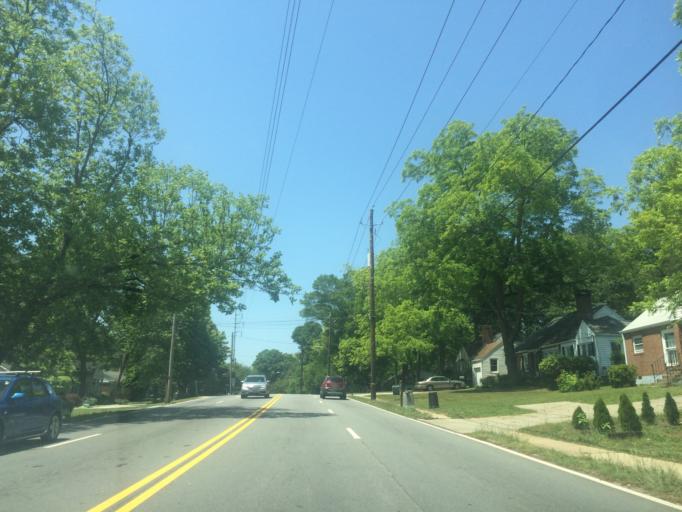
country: US
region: Georgia
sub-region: DeKalb County
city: North Decatur
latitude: 33.7938
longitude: -84.2929
